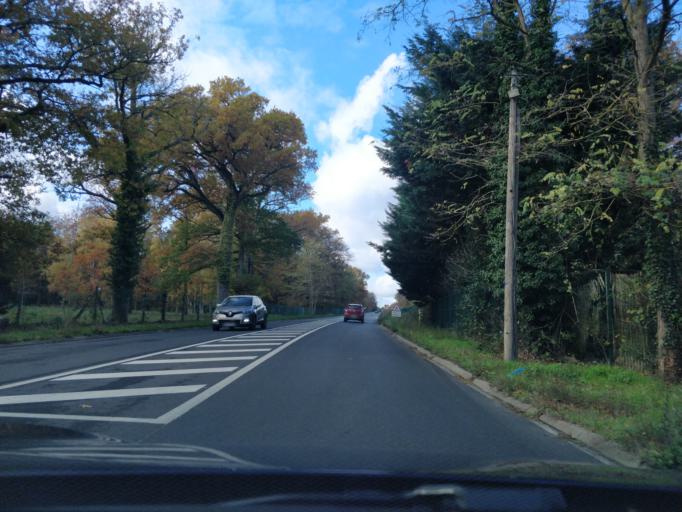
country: FR
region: Ile-de-France
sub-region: Departement de l'Essonne
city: Ollainville
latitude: 48.6039
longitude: 2.2084
